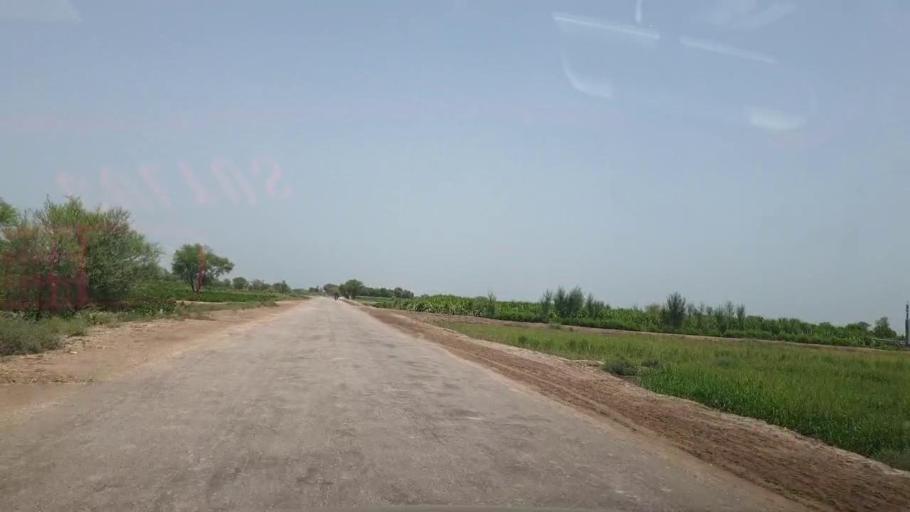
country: PK
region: Sindh
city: Daulatpur
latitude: 26.3894
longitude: 68.0919
